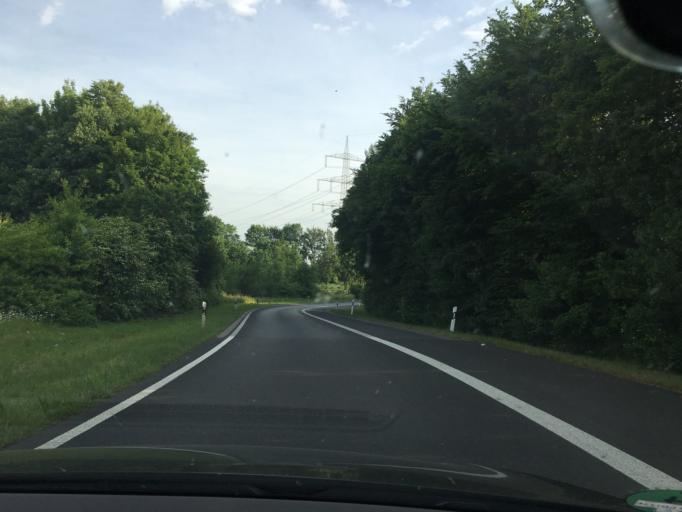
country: DE
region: North Rhine-Westphalia
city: Julich
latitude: 50.9142
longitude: 6.3260
